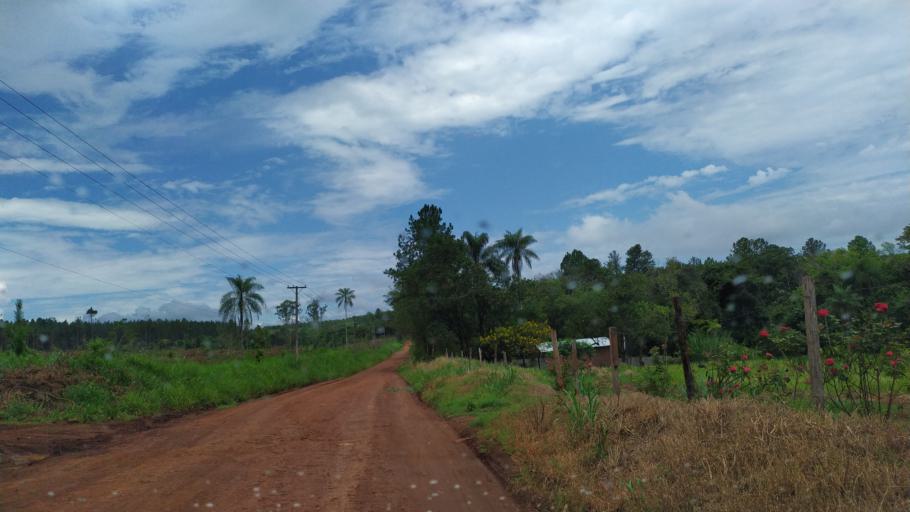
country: AR
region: Misiones
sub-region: Departamento de Eldorado
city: Eldorado
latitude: -26.4396
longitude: -54.6042
